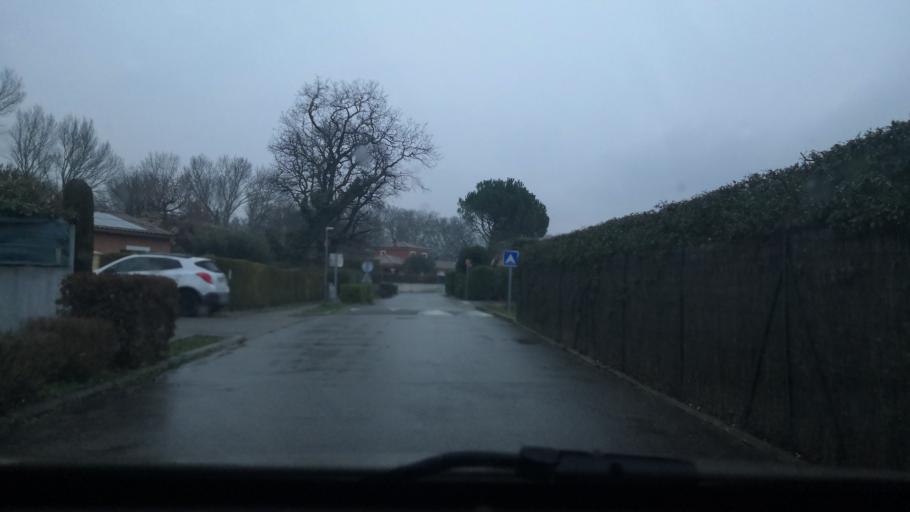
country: FR
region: Rhone-Alpes
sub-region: Departement de la Drome
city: Montboucher-sur-Jabron
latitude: 44.5440
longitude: 4.8004
